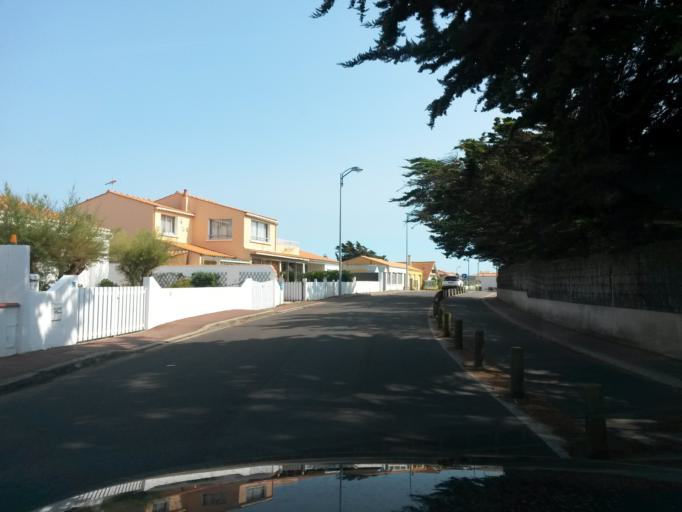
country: FR
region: Pays de la Loire
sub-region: Departement de la Vendee
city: Bretignolles-sur-Mer
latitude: 46.6284
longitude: -1.8751
